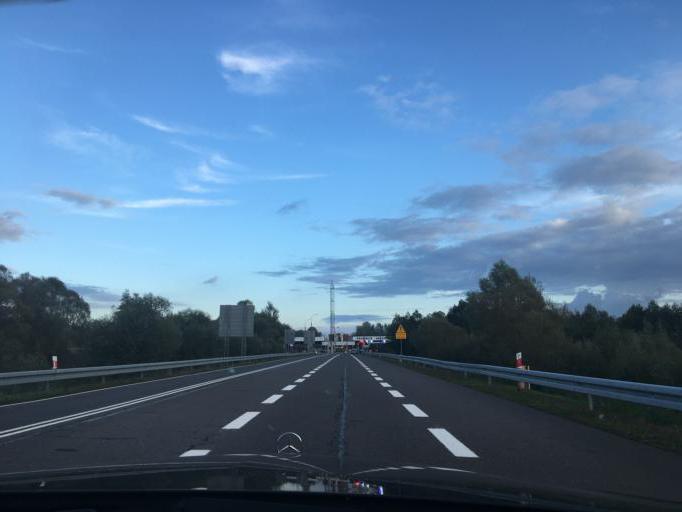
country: PL
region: Lublin Voivodeship
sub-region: Powiat bialski
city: Slawatycze
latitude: 51.7685
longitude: 23.5816
